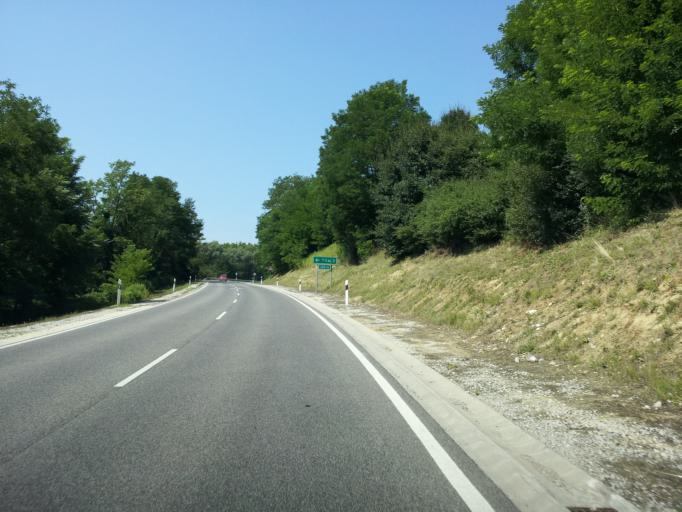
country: HU
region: Zala
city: Pacsa
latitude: 46.8085
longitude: 17.0767
